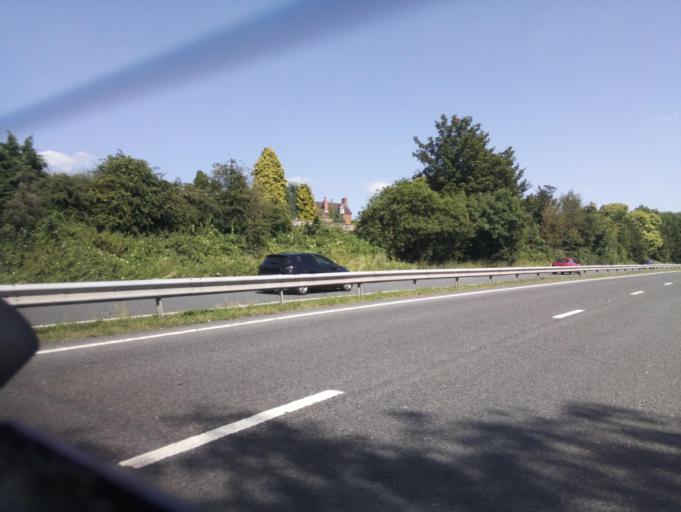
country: GB
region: England
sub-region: Worcestershire
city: Barnt Green
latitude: 52.3287
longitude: -2.0178
